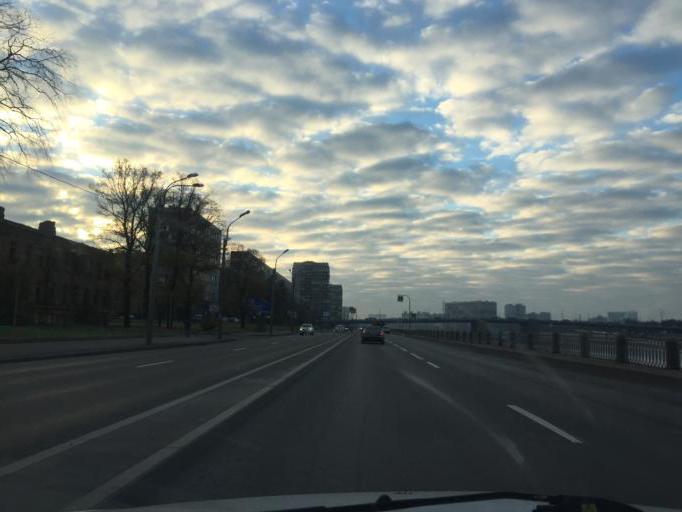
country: RU
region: St.-Petersburg
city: Obukhovo
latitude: 59.8835
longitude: 30.4504
